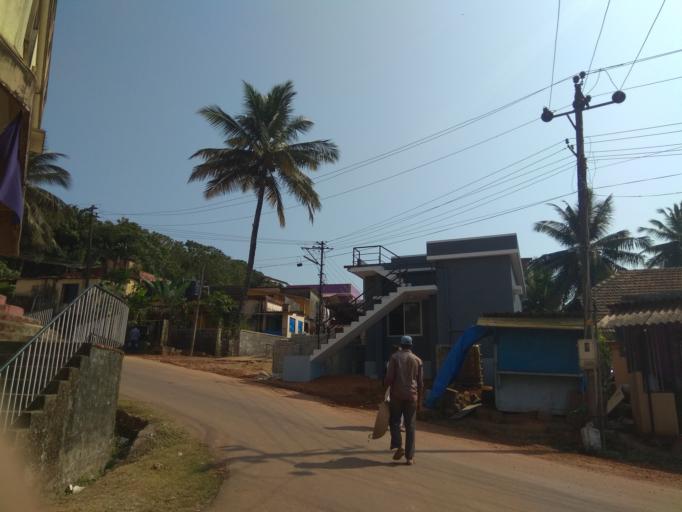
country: IN
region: Karnataka
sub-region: Dakshina Kannada
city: Mangalore
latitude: 12.9407
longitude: 74.8516
